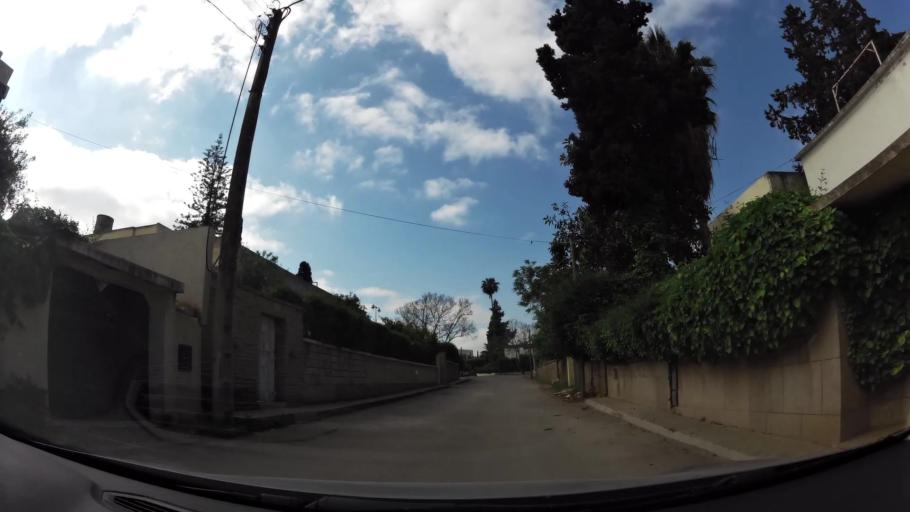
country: MA
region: Fes-Boulemane
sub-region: Fes
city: Fes
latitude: 34.0319
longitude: -5.0108
